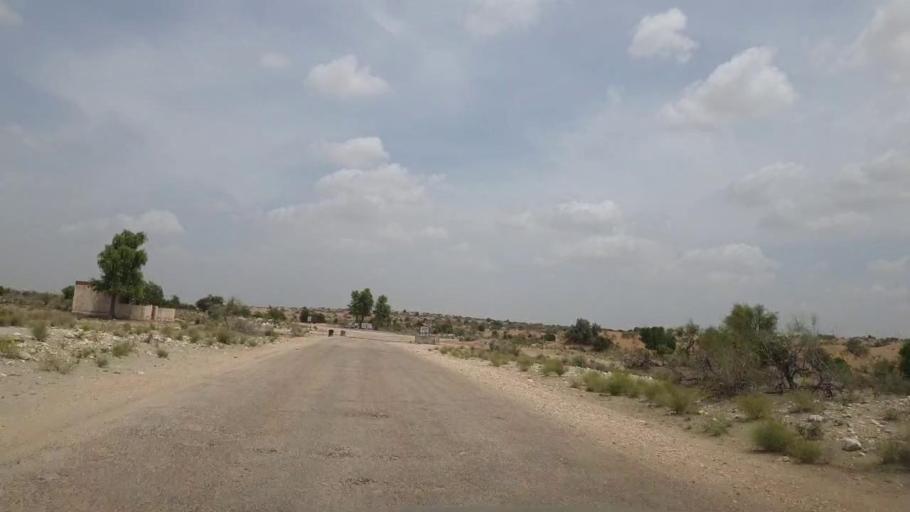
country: PK
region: Sindh
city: Kot Diji
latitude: 27.1659
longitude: 69.2210
